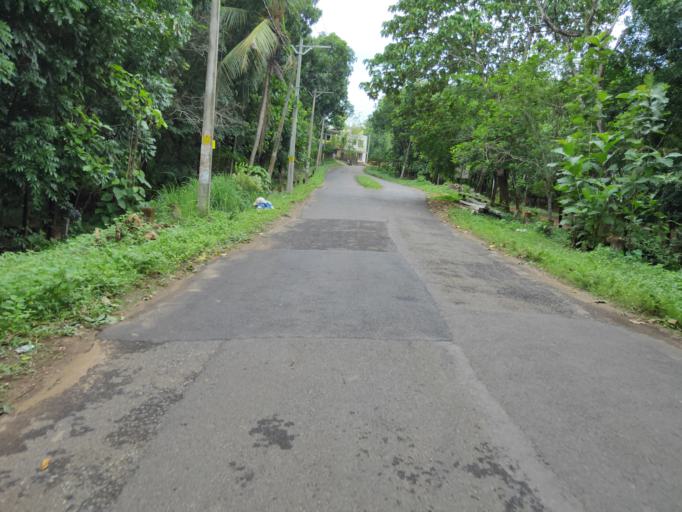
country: IN
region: Kerala
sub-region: Malappuram
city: Manjeri
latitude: 11.2637
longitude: 76.2397
